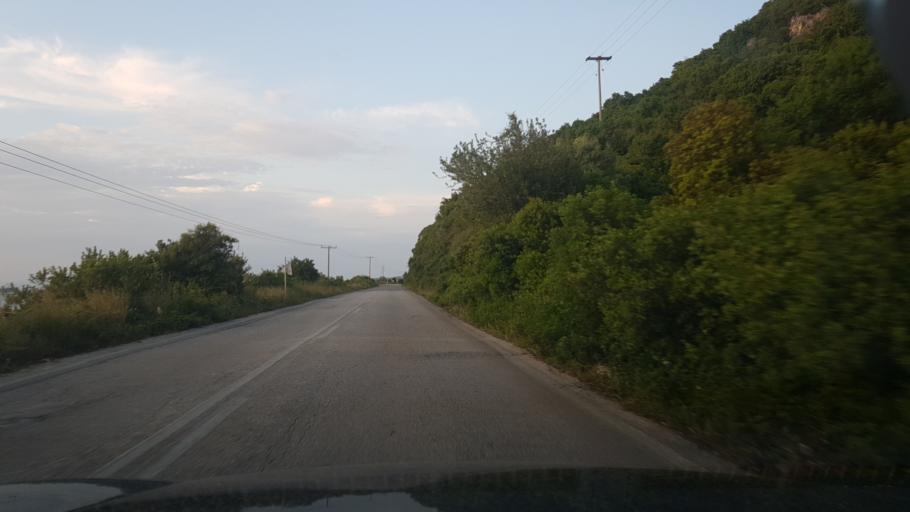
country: GR
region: Ionian Islands
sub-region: Lefkada
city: Lefkada
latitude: 38.8558
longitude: 20.7494
